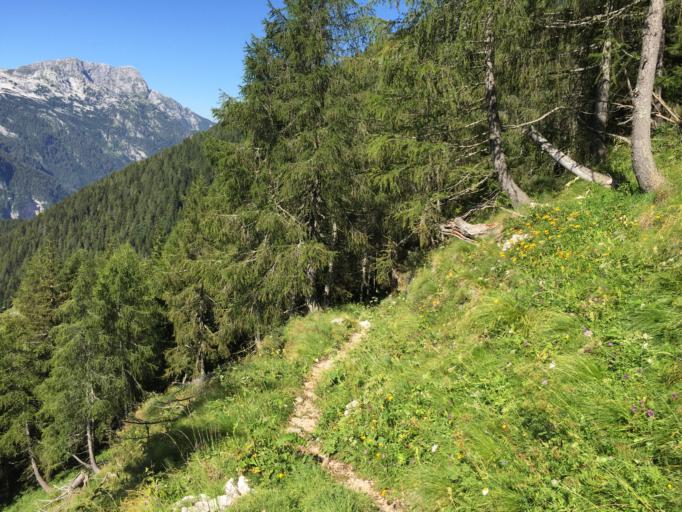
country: SI
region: Bovec
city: Bovec
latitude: 46.4035
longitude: 13.4846
